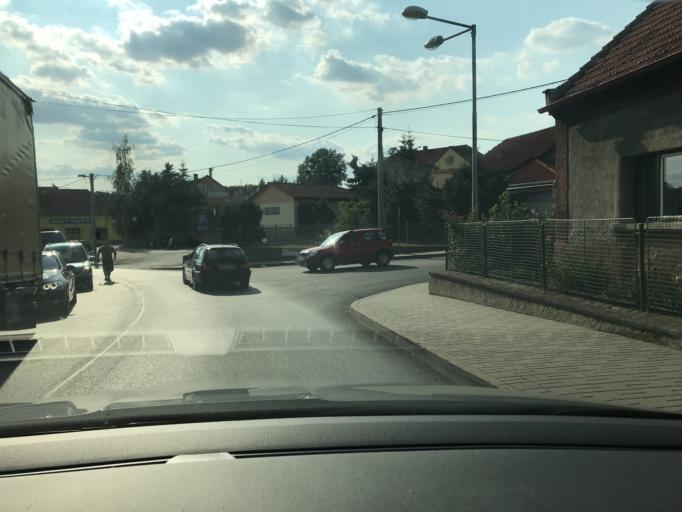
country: CZ
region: Central Bohemia
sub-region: Okres Kladno
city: Slany
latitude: 50.2468
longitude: 14.1420
